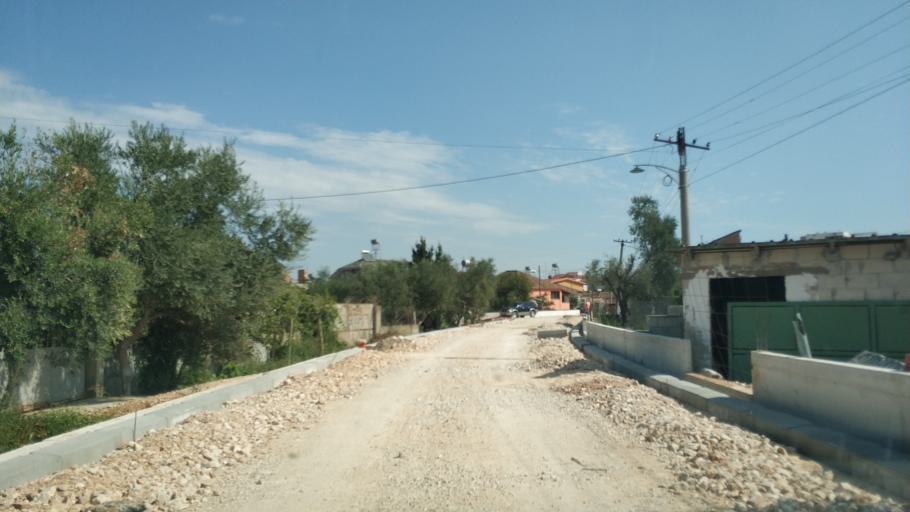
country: AL
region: Fier
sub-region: Rrethi i Lushnjes
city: Divjake
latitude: 40.9933
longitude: 19.5265
